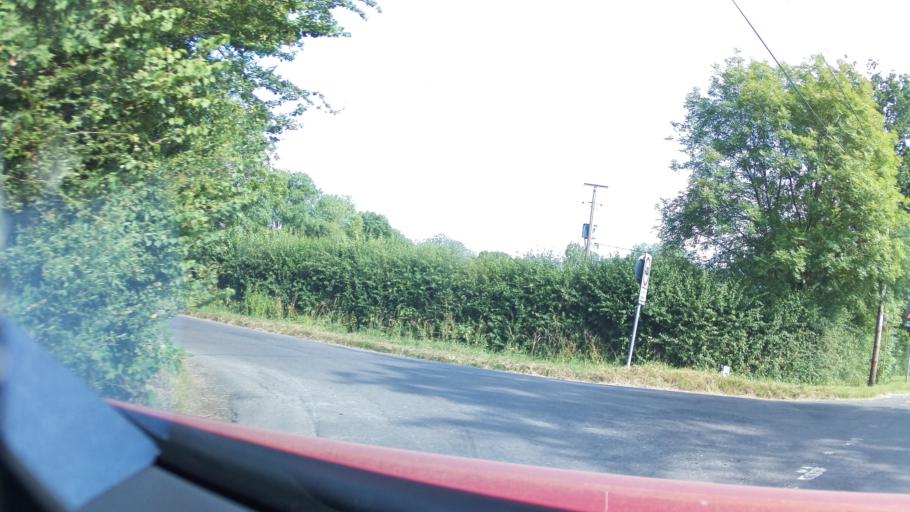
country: GB
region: England
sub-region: Wiltshire
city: Minety
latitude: 51.6215
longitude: -1.9672
